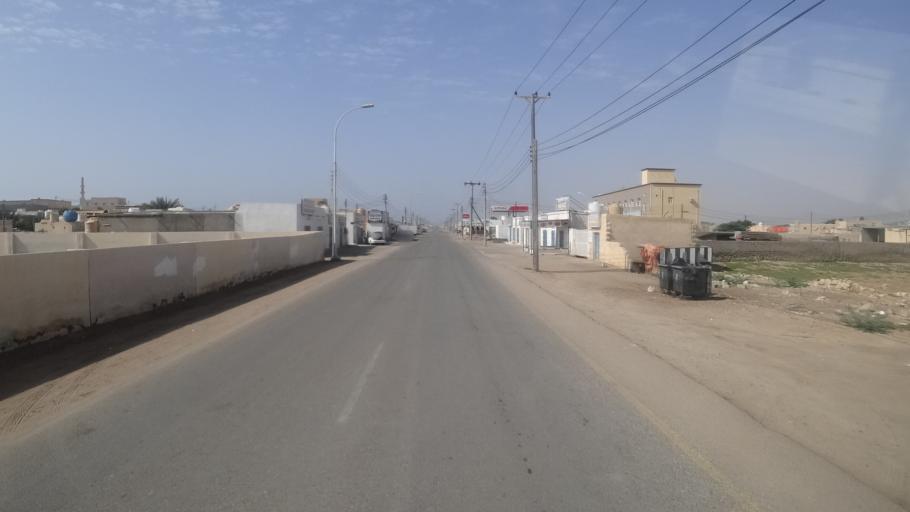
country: OM
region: Ash Sharqiyah
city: Sur
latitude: 22.1809
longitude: 59.7628
